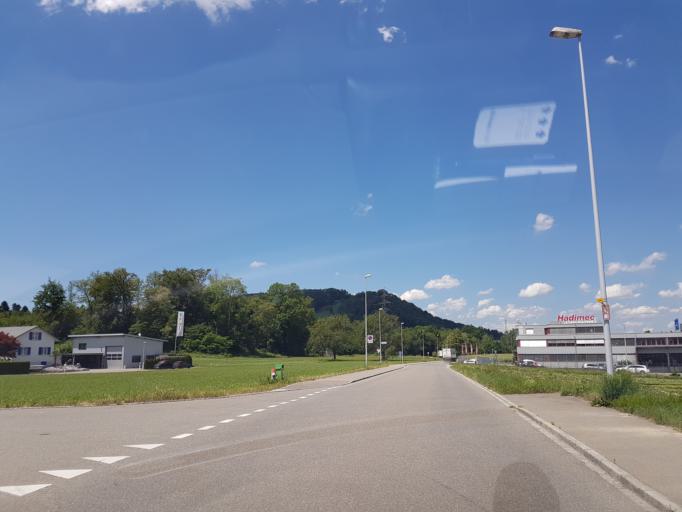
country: CH
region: Aargau
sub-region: Bezirk Lenzburg
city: Othmarsingen
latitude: 47.4127
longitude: 8.2262
